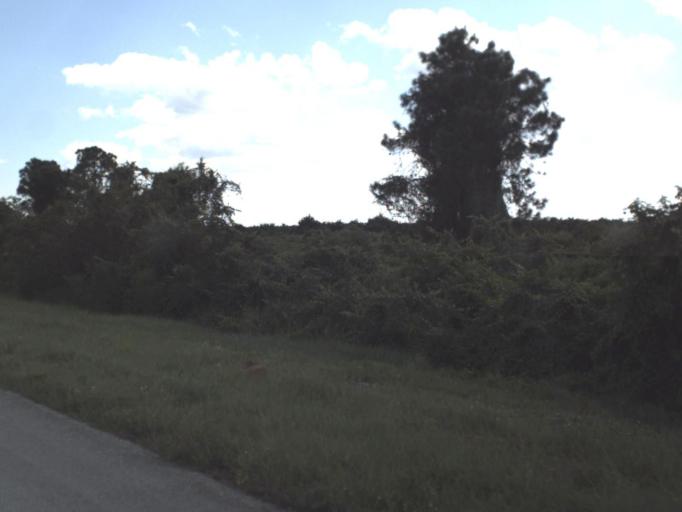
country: US
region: Florida
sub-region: Highlands County
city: Lake Placid
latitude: 27.3861
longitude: -81.1363
